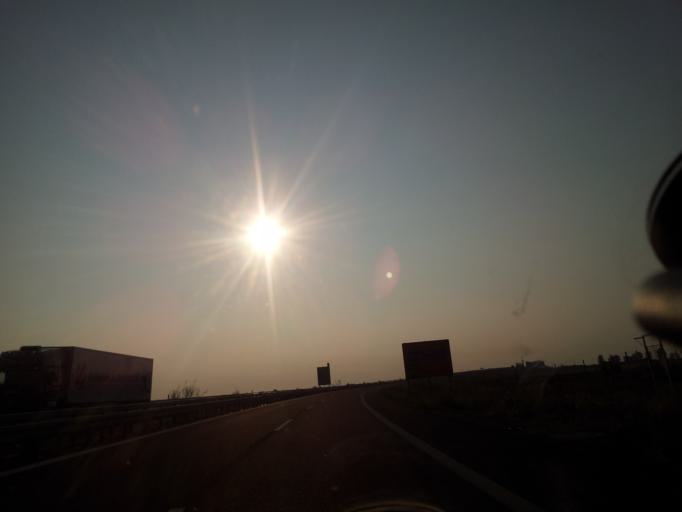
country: DE
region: Saxony-Anhalt
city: Ilberstedt
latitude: 51.8114
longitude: 11.6556
